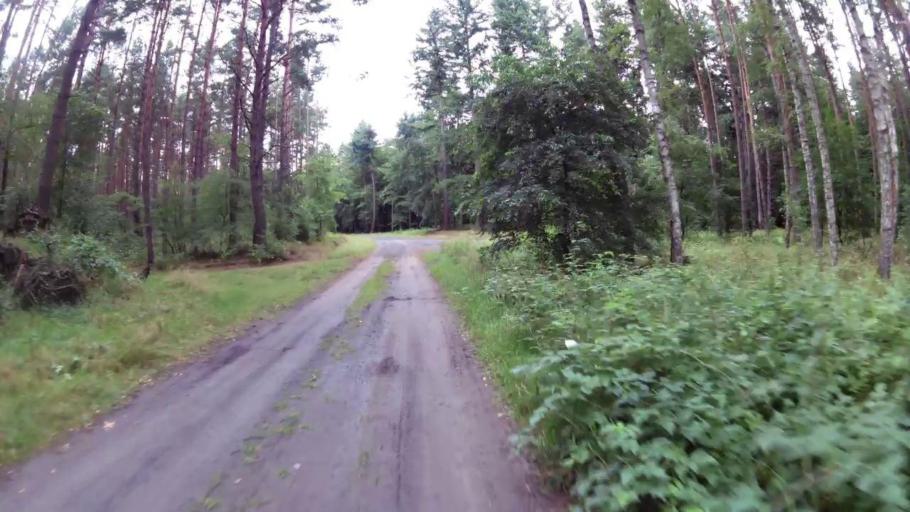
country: PL
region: West Pomeranian Voivodeship
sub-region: Powiat mysliborski
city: Debno
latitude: 52.7867
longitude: 14.7177
